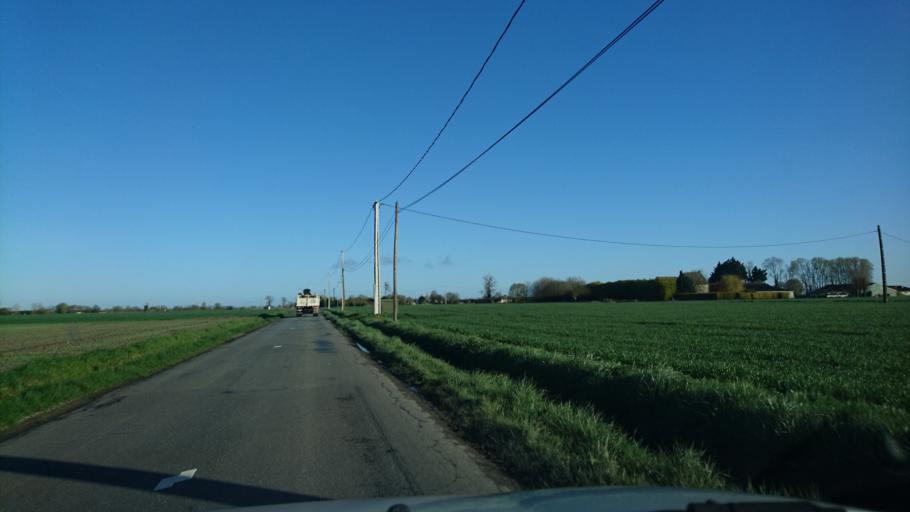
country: FR
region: Brittany
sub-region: Departement d'Ille-et-Vilaine
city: Cherrueix
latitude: 48.5841
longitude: -1.7161
